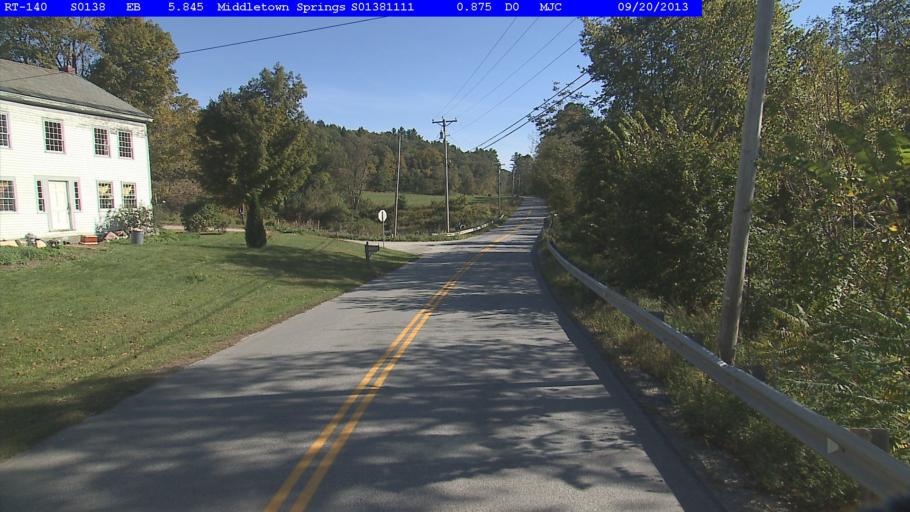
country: US
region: Vermont
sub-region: Rutland County
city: Poultney
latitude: 43.4942
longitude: -73.1554
